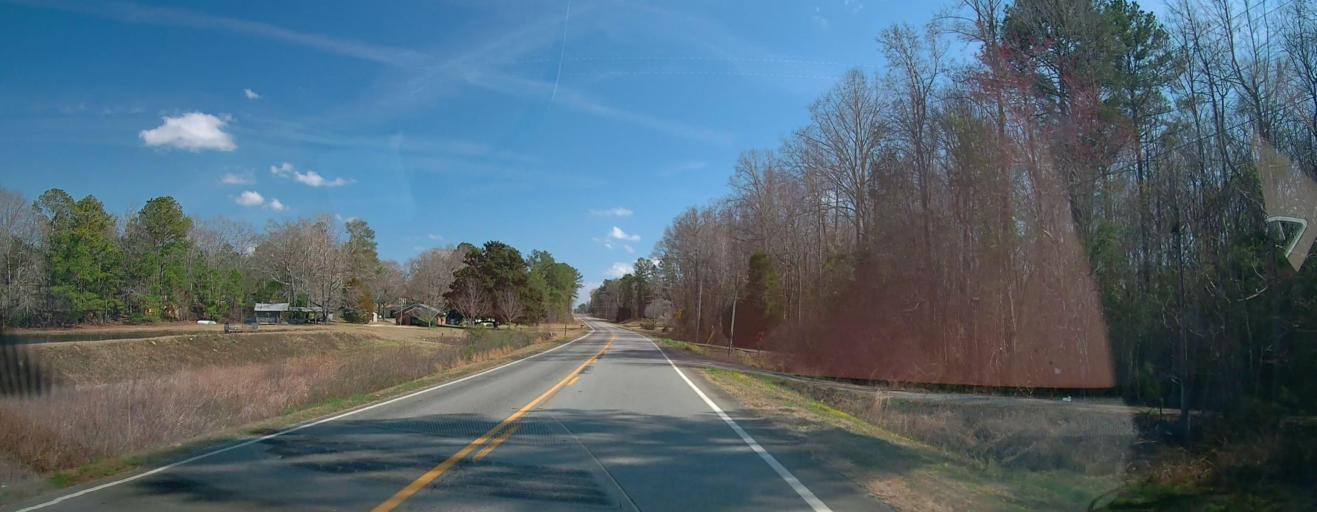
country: US
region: Georgia
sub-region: Wilkinson County
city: Gordon
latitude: 32.9022
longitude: -83.3722
